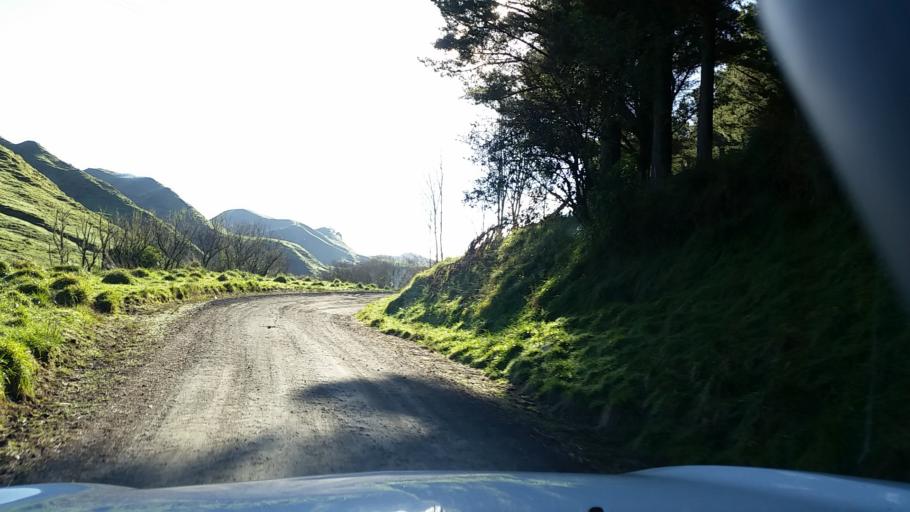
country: NZ
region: Taranaki
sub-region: South Taranaki District
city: Eltham
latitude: -39.5043
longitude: 174.4032
